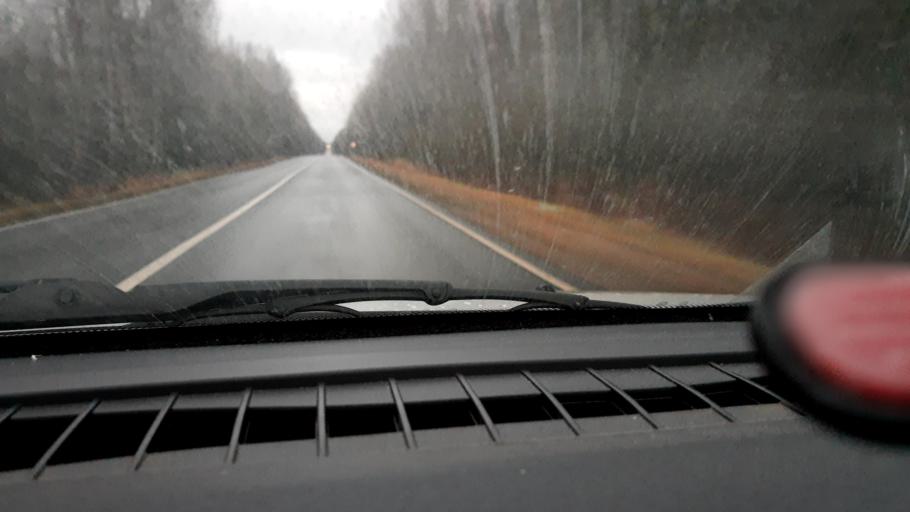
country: RU
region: Nizjnij Novgorod
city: Uren'
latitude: 57.2515
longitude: 45.6049
